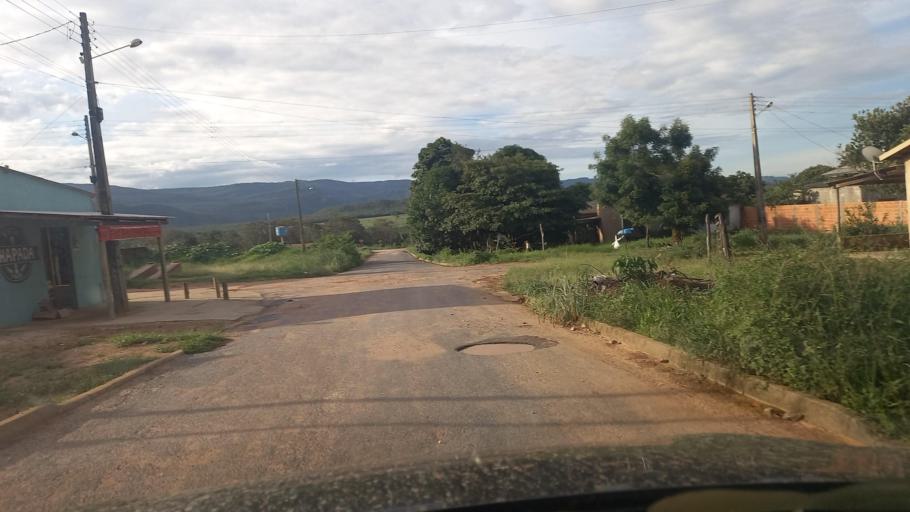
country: BR
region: Goias
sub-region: Cavalcante
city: Cavalcante
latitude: -13.7958
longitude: -47.4449
